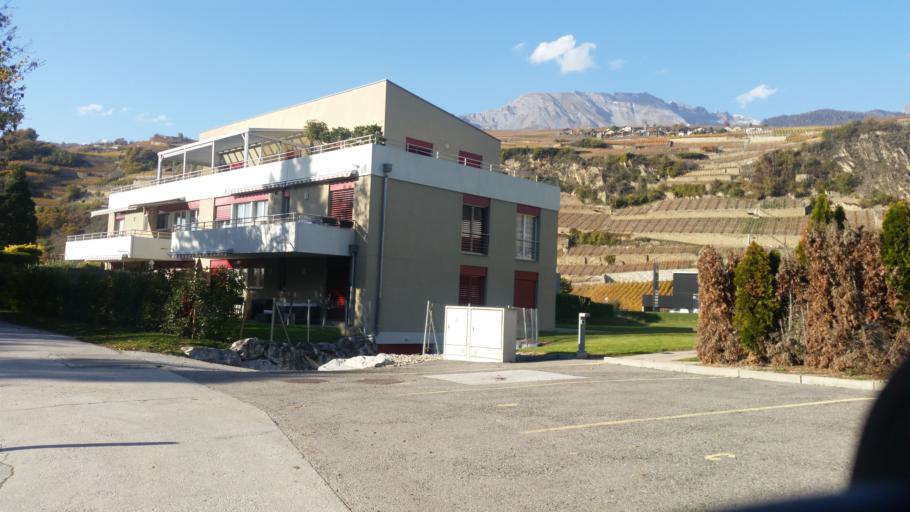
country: CH
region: Valais
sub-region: Sion District
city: Saint-Leonard
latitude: 46.2500
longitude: 7.4083
